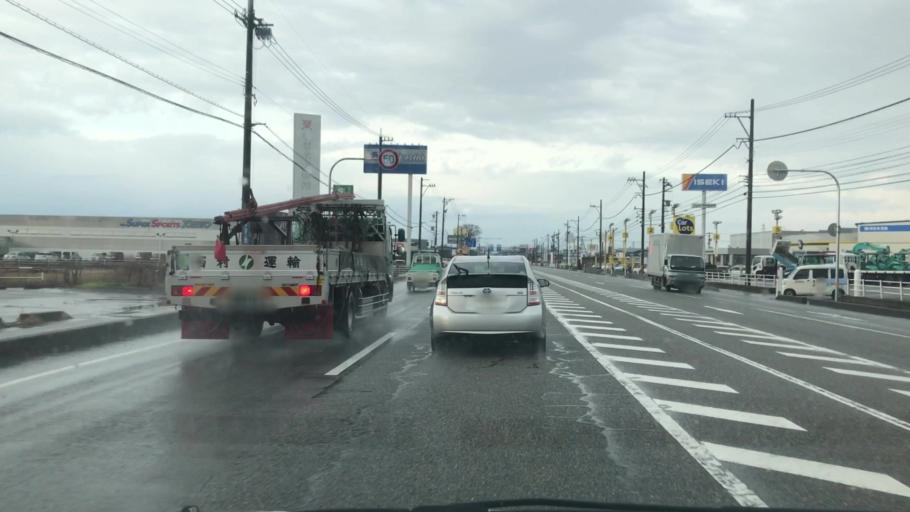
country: JP
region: Toyama
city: Toyama-shi
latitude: 36.6397
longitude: 137.2093
